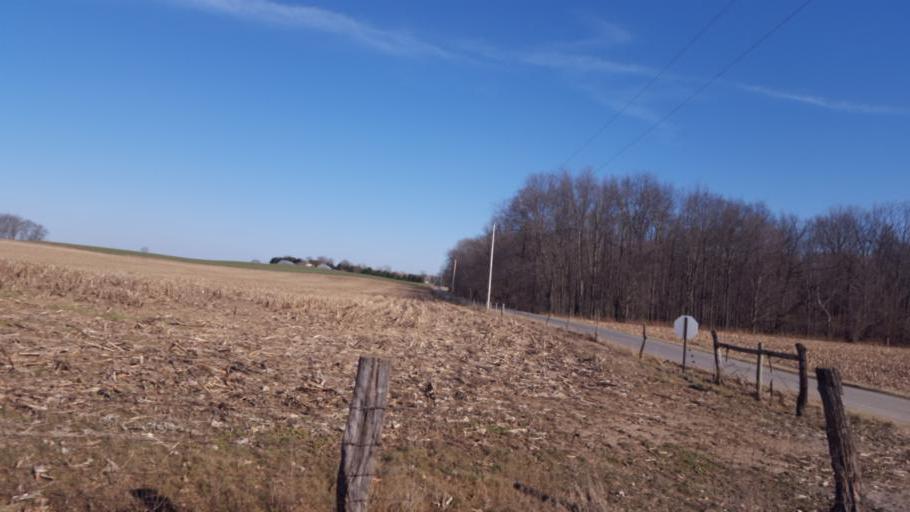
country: US
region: Ohio
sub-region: Knox County
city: Fredericktown
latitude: 40.5200
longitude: -82.6286
